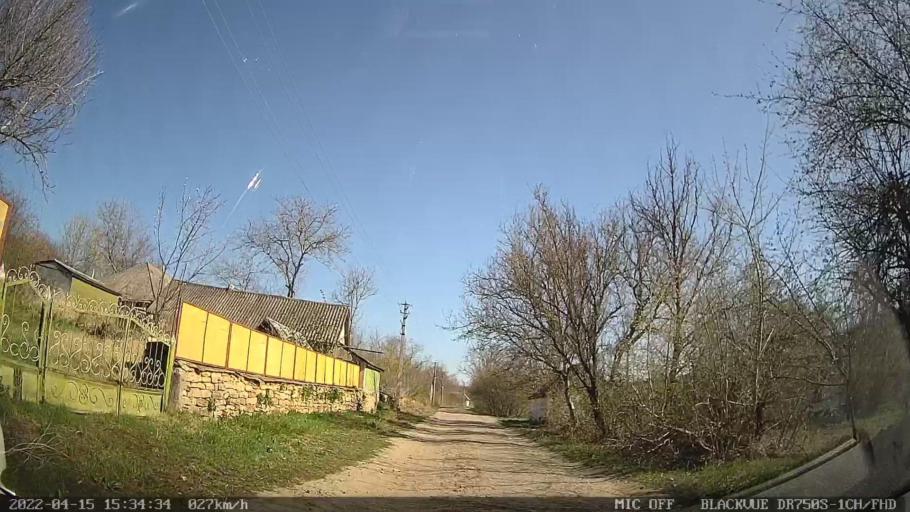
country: MD
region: Raionul Ocnita
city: Otaci
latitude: 48.3471
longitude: 27.9279
